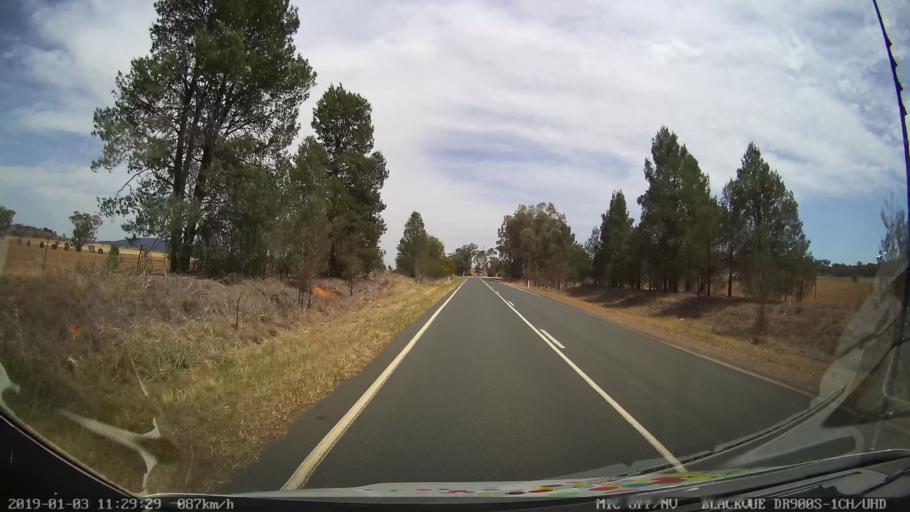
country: AU
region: New South Wales
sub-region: Weddin
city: Grenfell
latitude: -33.9919
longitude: 148.1979
